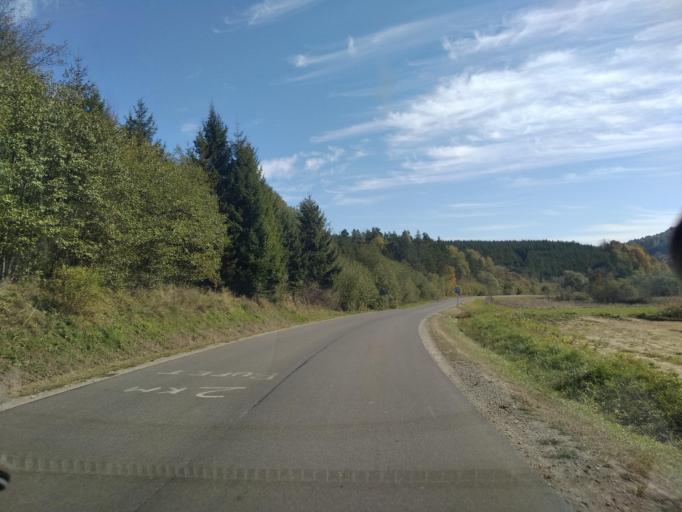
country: PL
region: Subcarpathian Voivodeship
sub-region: Powiat sanocki
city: Komancza
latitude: 49.3448
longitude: 22.0351
